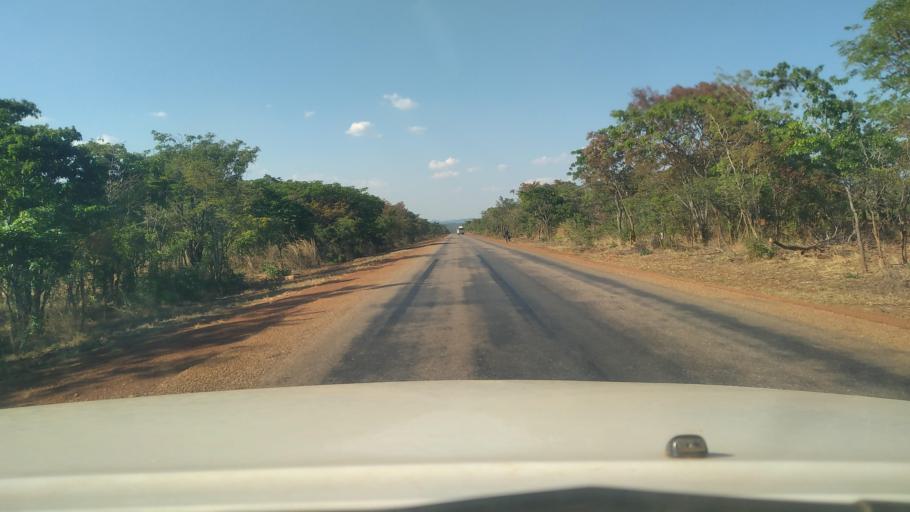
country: ZM
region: Northern
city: Mpika
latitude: -11.7687
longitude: 31.4623
